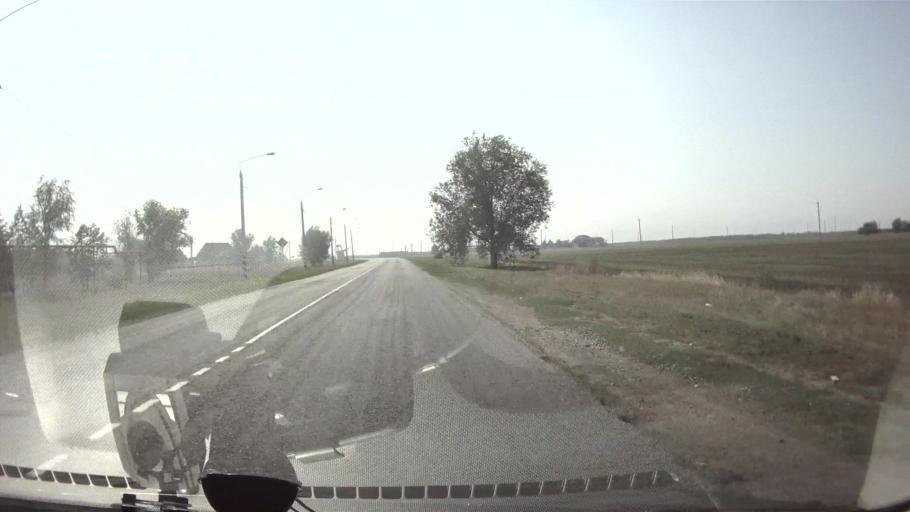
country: RU
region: Krasnodarskiy
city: Novopokrovskaya
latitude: 45.9288
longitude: 40.7104
